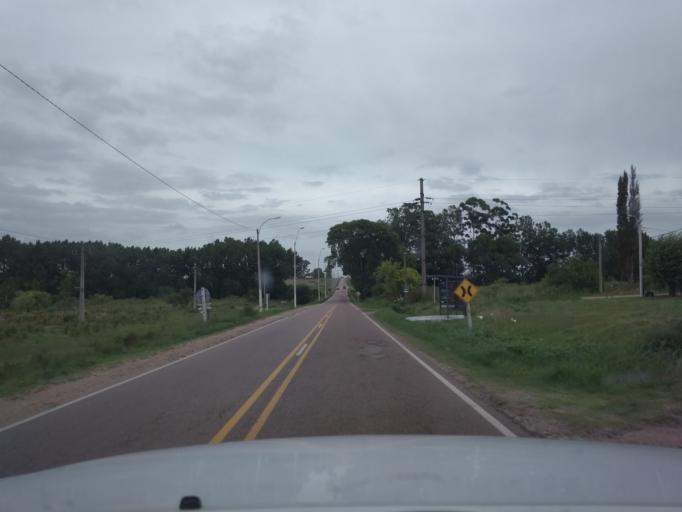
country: UY
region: Canelones
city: Tala
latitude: -34.3536
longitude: -55.7699
